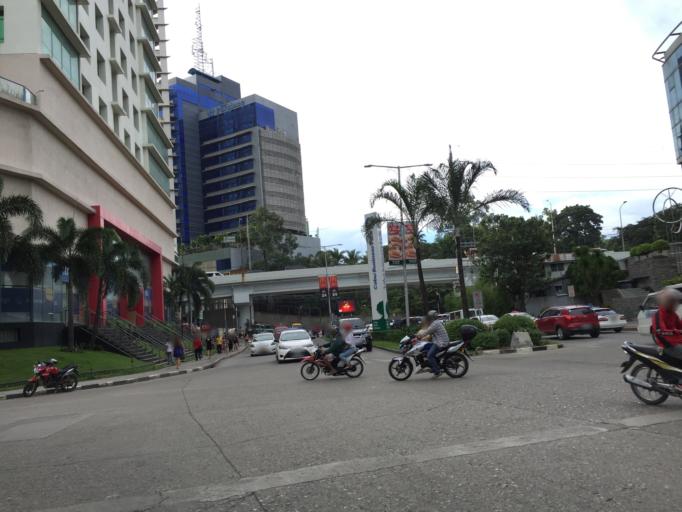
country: PH
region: Central Visayas
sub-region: Province of Cebu
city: Cebu City
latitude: 10.3200
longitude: 123.9046
